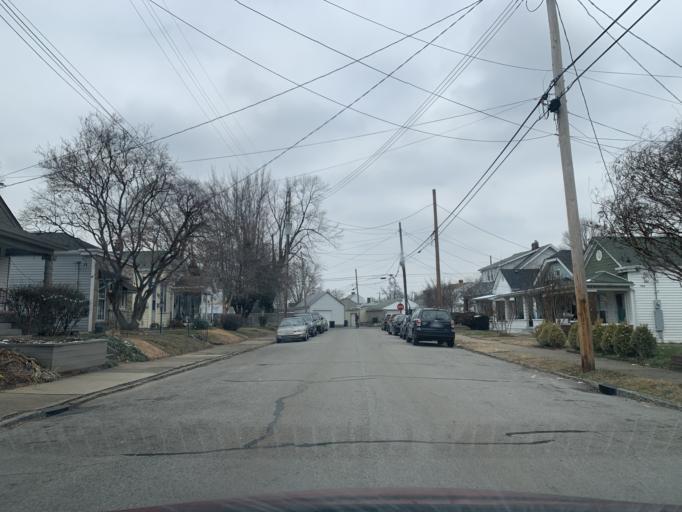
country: US
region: Kentucky
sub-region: Jefferson County
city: Audubon Park
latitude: 38.2232
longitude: -85.7351
